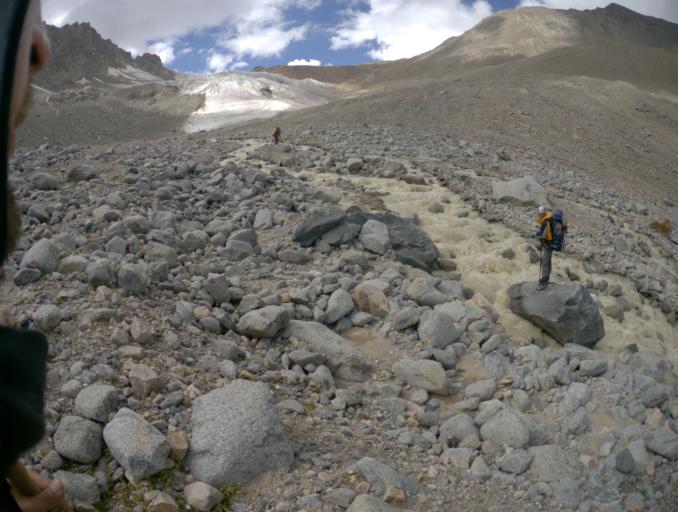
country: RU
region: Kabardino-Balkariya
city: Terskol
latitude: 43.3343
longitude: 42.5507
